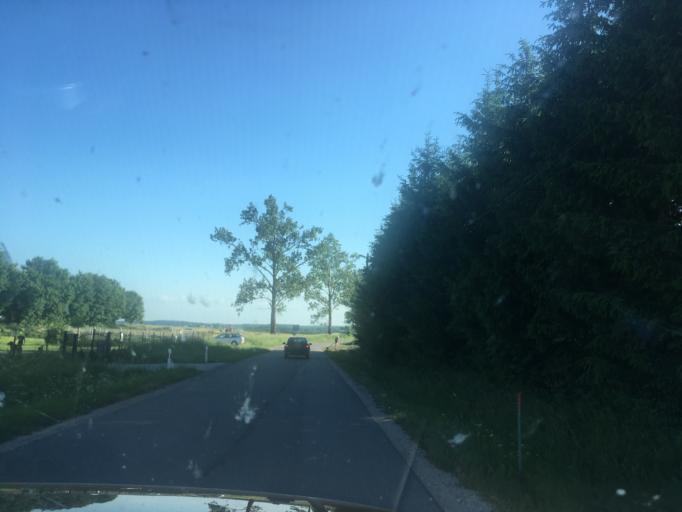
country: PL
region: Warmian-Masurian Voivodeship
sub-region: Powiat ostrodzki
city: Ostroda
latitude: 53.6768
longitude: 20.0418
